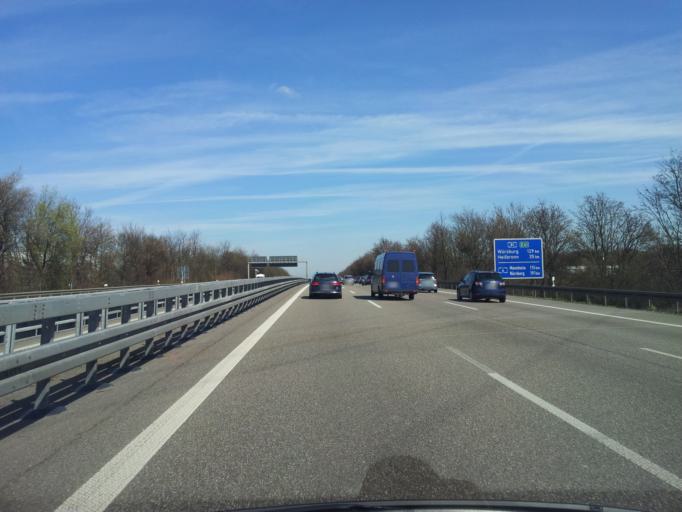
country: DE
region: Baden-Wuerttemberg
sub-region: Regierungsbezirk Stuttgart
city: Asperg
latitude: 48.8899
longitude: 9.1482
